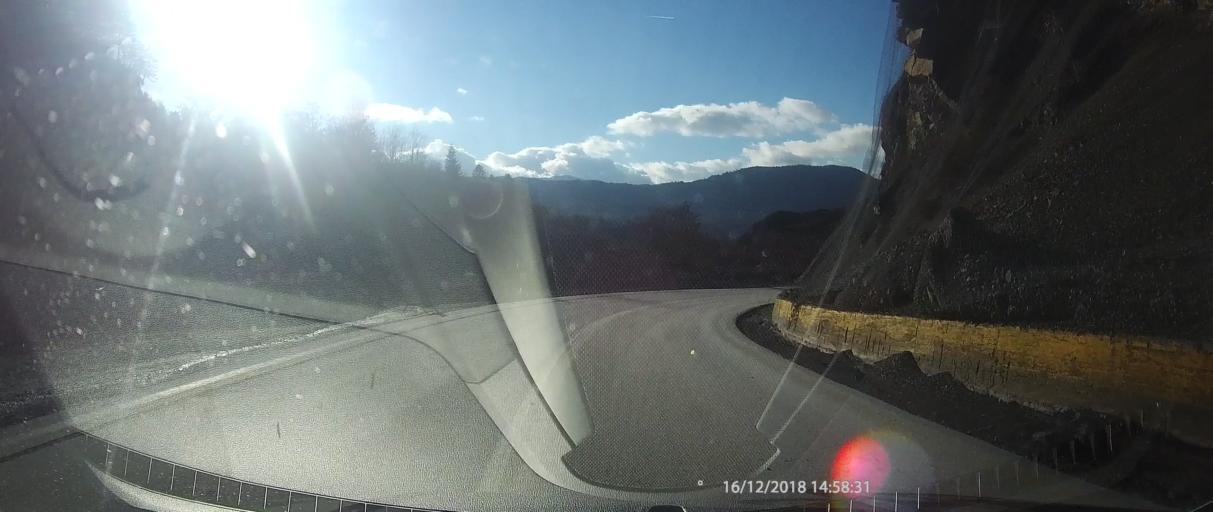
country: GR
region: West Macedonia
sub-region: Nomos Kastorias
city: Nestorio
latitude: 40.2229
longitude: 21.0301
